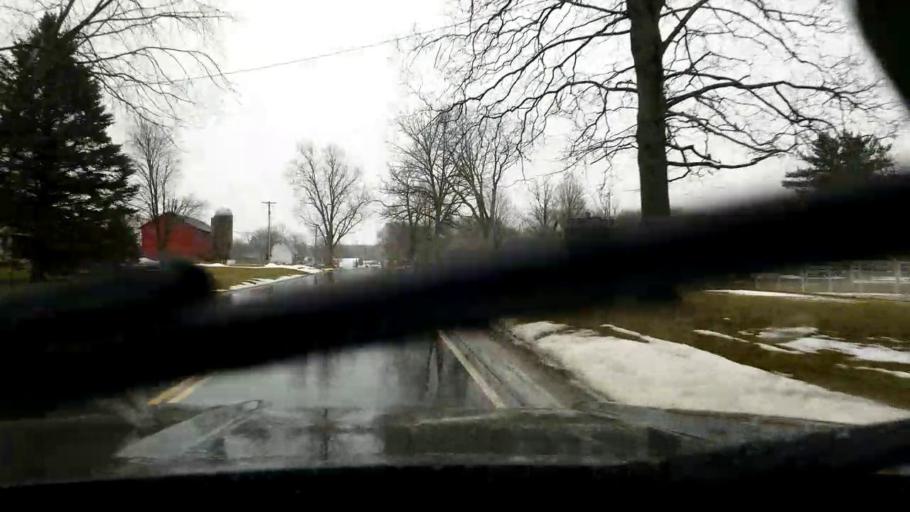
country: US
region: Michigan
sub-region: Jackson County
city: Michigan Center
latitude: 42.3104
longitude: -84.3094
